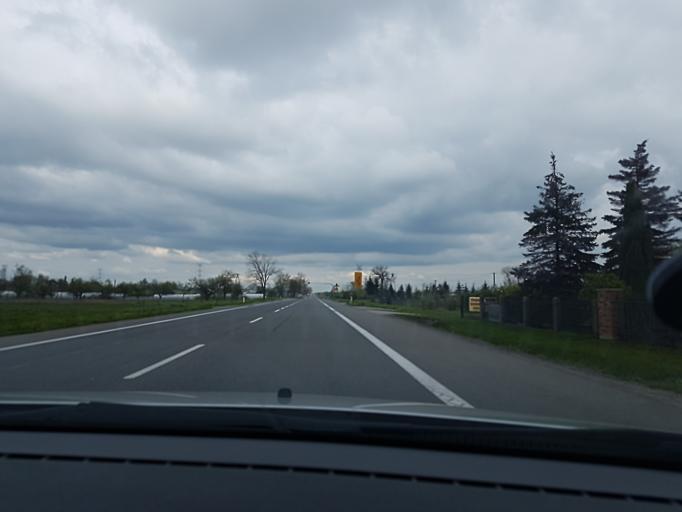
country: PL
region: Lodz Voivodeship
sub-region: powiat Lowicki
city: Lowicz
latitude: 52.1199
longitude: 19.9877
